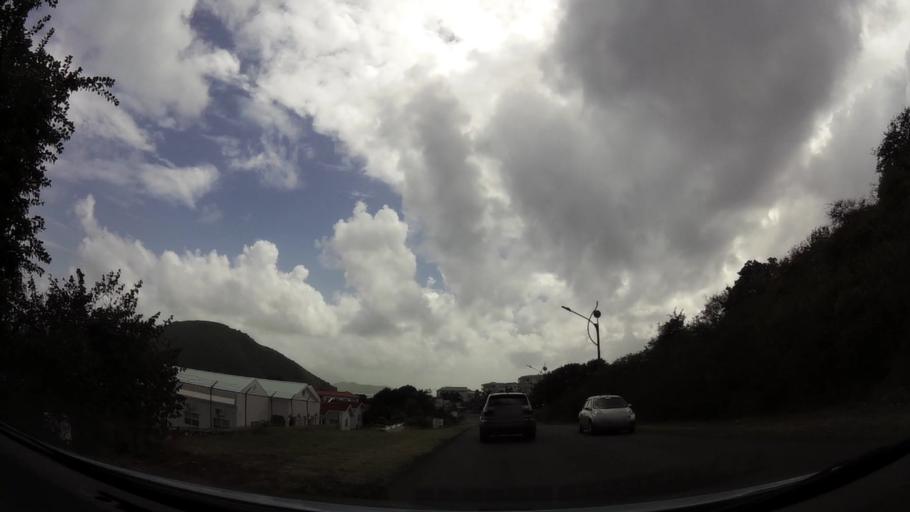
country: KN
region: Saint George Basseterre
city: Basseterre
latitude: 17.2875
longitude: -62.6927
